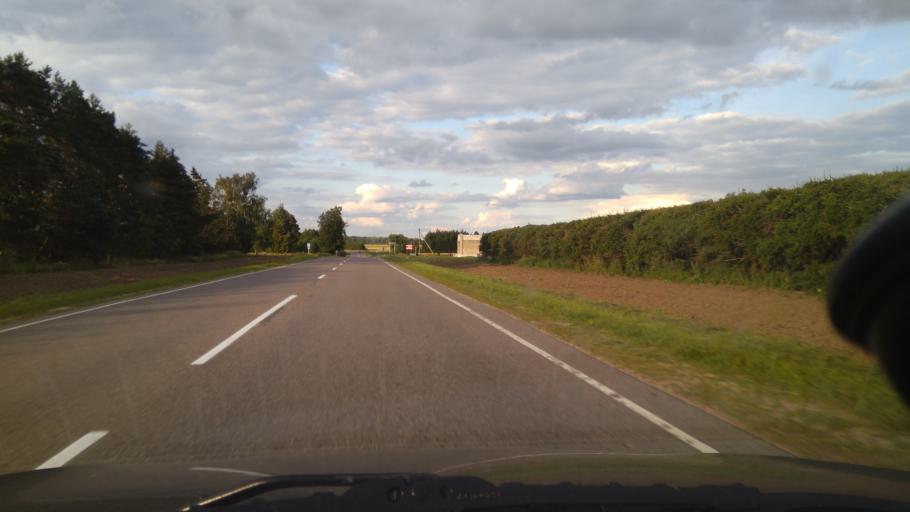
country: BY
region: Grodnenskaya
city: Shchuchin
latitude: 53.5129
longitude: 24.6911
